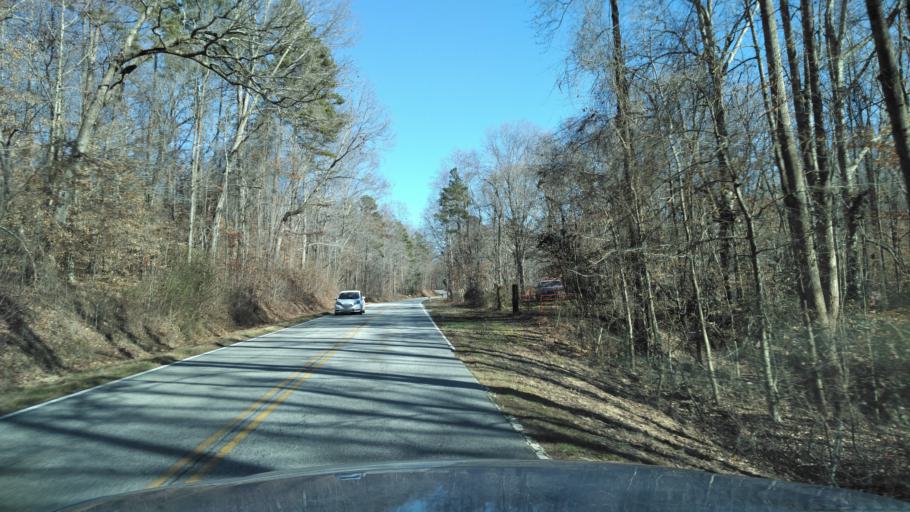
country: US
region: Georgia
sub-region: Hall County
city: Lula
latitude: 34.3180
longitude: -83.6858
